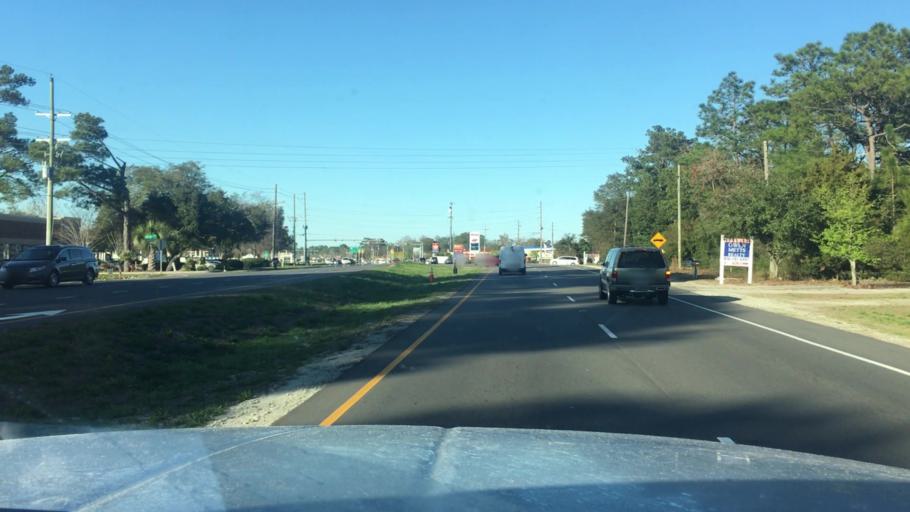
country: US
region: North Carolina
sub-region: New Hanover County
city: Myrtle Grove
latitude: 34.1322
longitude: -77.8958
